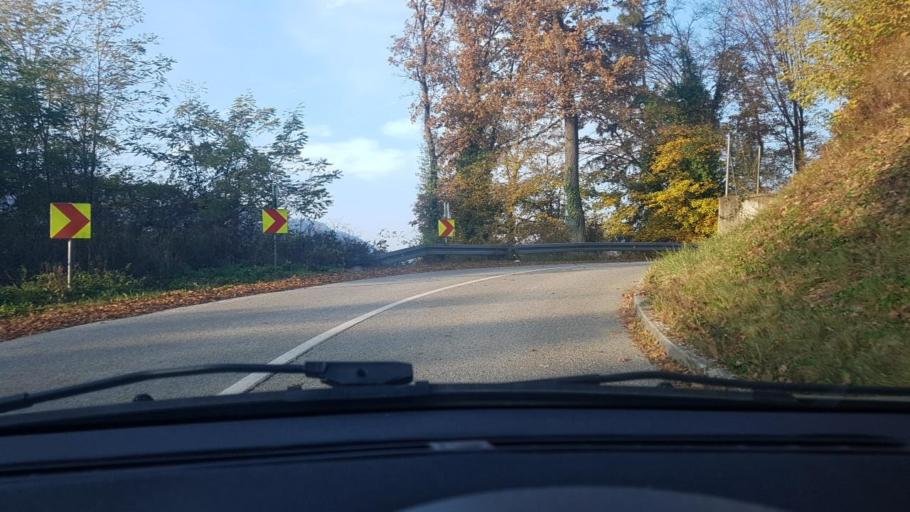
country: SI
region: Podcetrtek
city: Podcetrtek
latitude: 46.1474
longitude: 15.5980
